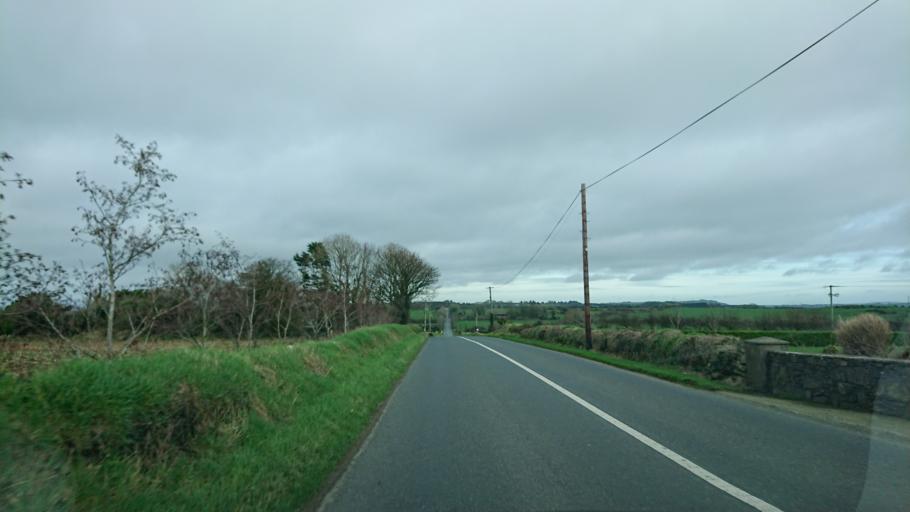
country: IE
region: Munster
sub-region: Waterford
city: Portlaw
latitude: 52.1869
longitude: -7.2920
